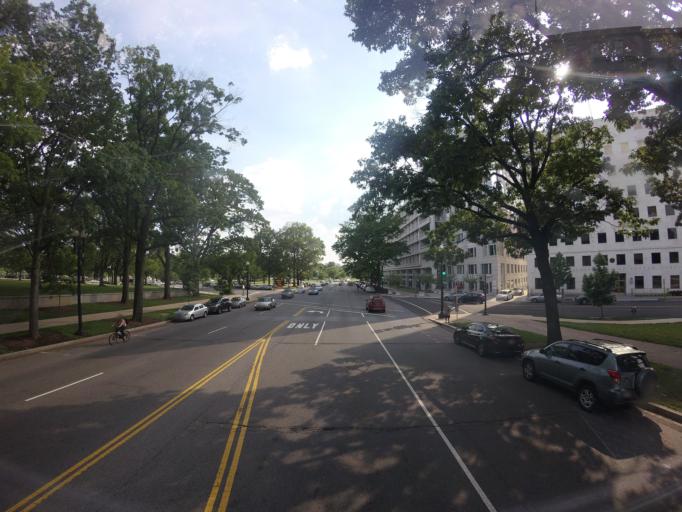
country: US
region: Washington, D.C.
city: Washington, D.C.
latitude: 38.8932
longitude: -77.0117
